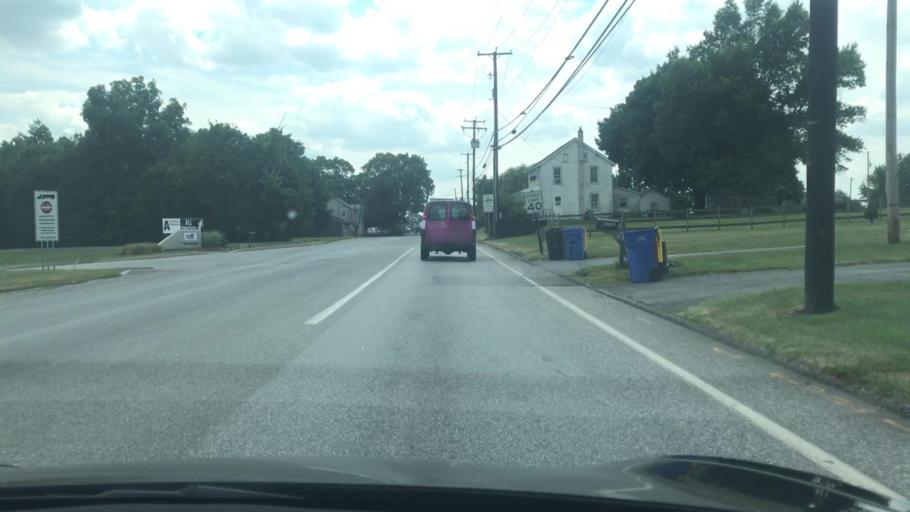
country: US
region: Pennsylvania
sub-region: York County
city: Manchester
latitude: 40.0716
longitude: -76.7665
